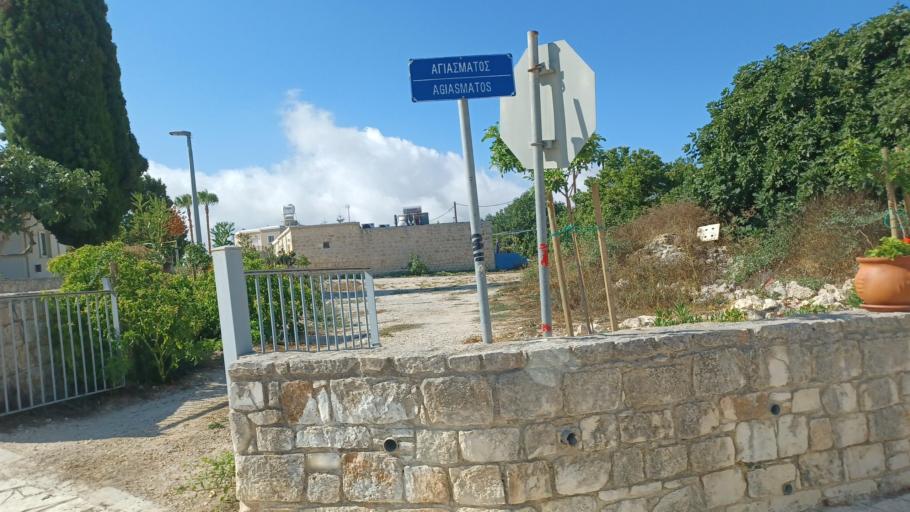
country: CY
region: Pafos
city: Pegeia
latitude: 34.9104
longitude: 32.4264
